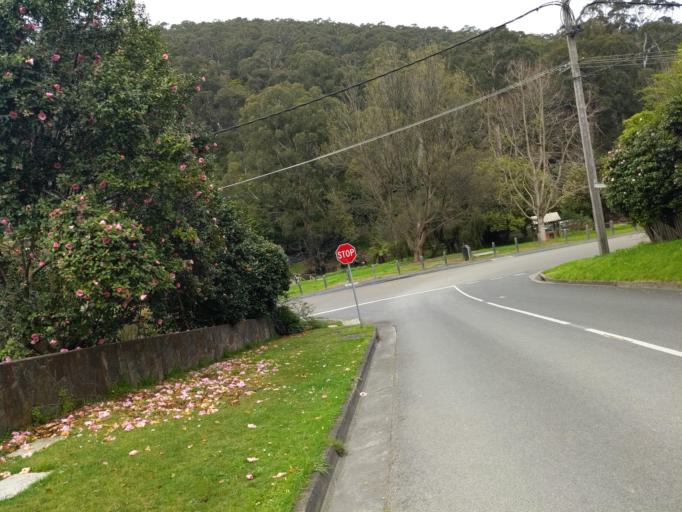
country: AU
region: Victoria
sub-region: Yarra Ranges
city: Millgrove
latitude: -37.7522
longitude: 145.6925
